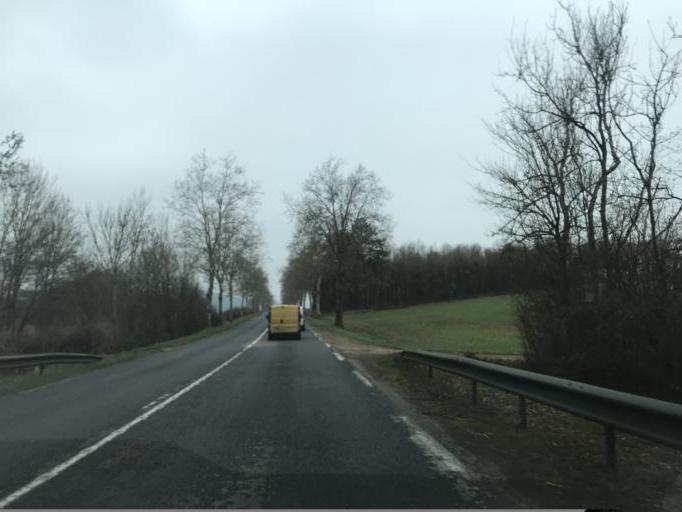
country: FR
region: Bourgogne
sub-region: Departement de l'Yonne
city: Avallon
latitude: 47.5028
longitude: 3.8800
